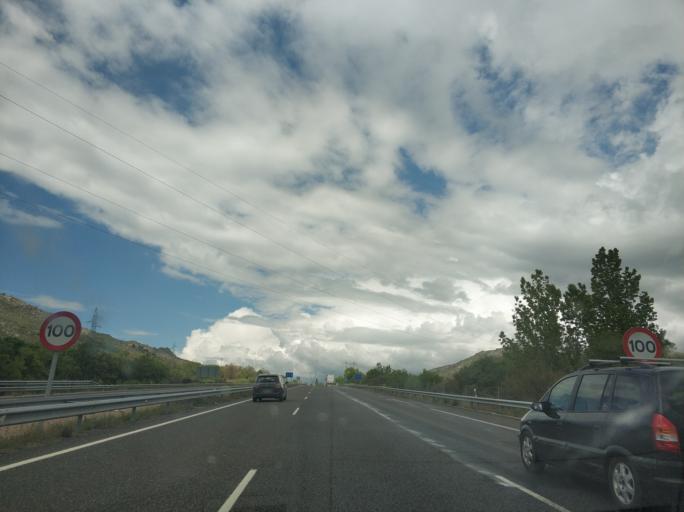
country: ES
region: Castille and Leon
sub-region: Provincia de Salamanca
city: Vallejera de Riofrio
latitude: 40.4056
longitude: -5.7286
